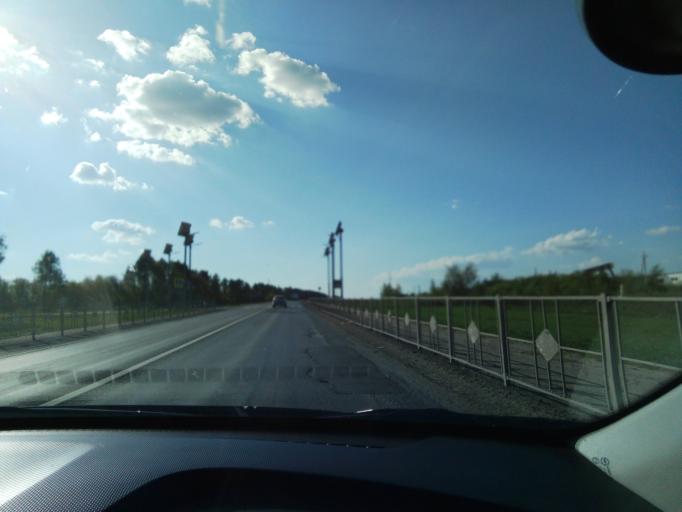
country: RU
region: Chuvashia
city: Novyye Lapsary
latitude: 56.0624
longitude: 47.2465
